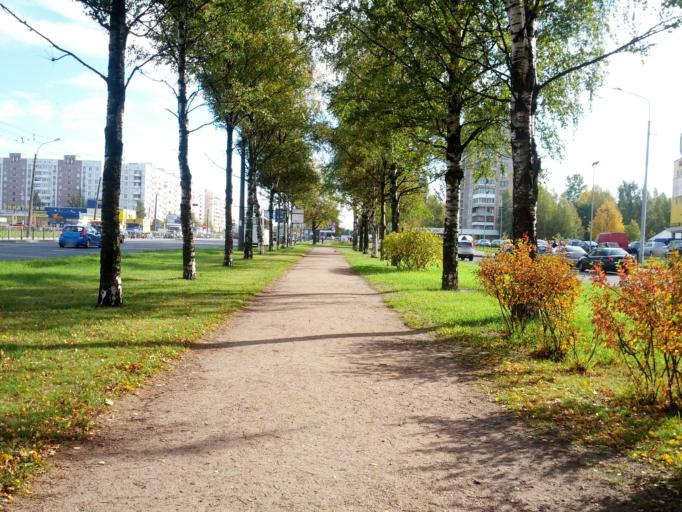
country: RU
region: Leningrad
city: Rybatskoye
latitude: 59.9016
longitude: 30.4871
